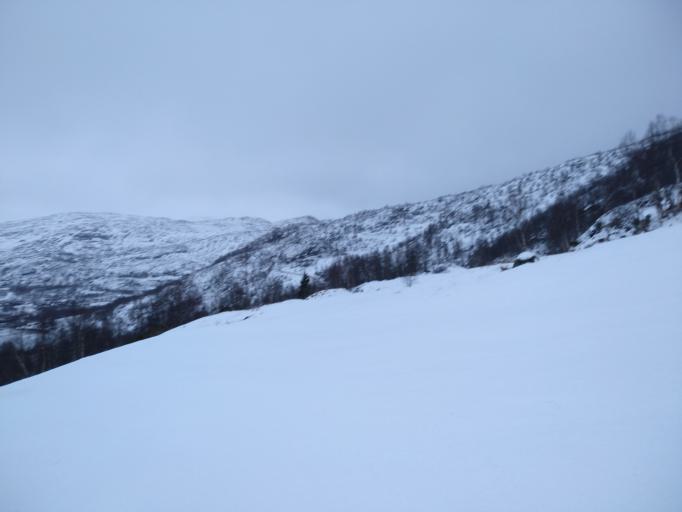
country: NO
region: Vest-Agder
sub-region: Sirdal
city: Tonstad
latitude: 59.0217
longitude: 6.9191
